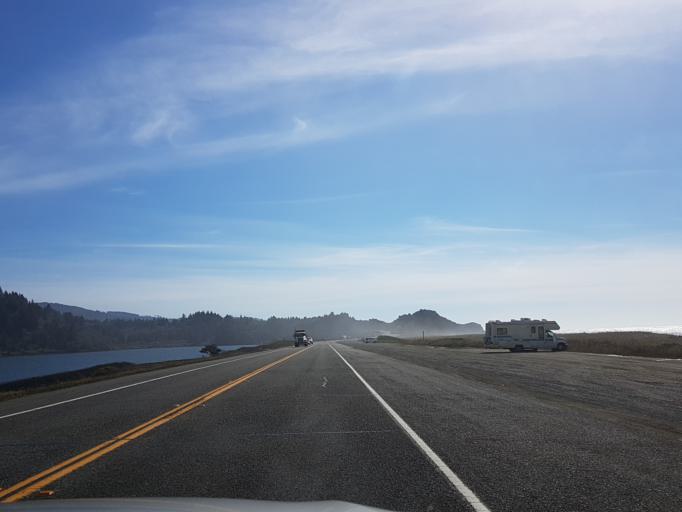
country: US
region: California
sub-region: Humboldt County
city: Westhaven-Moonstone
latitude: 41.2770
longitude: -124.0942
